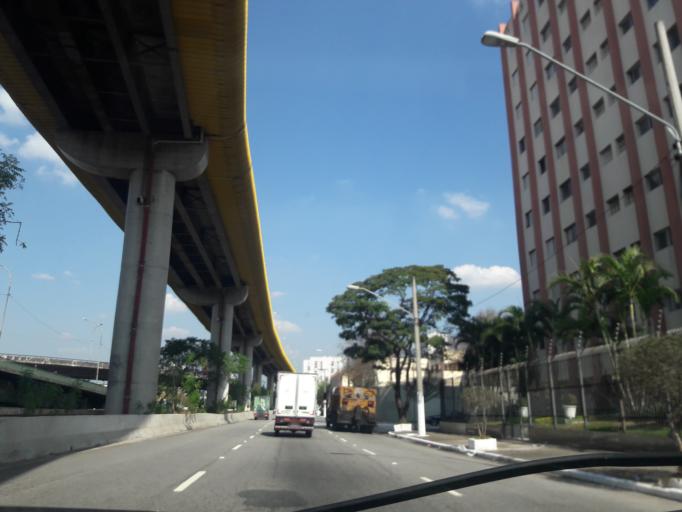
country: BR
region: Sao Paulo
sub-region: Sao Paulo
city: Sao Paulo
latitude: -23.5871
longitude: -46.5984
